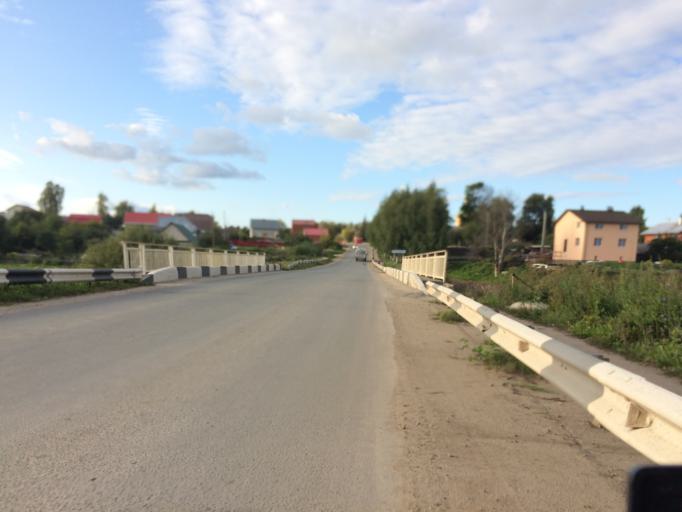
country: RU
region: Mariy-El
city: Yoshkar-Ola
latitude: 56.6481
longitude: 47.9810
